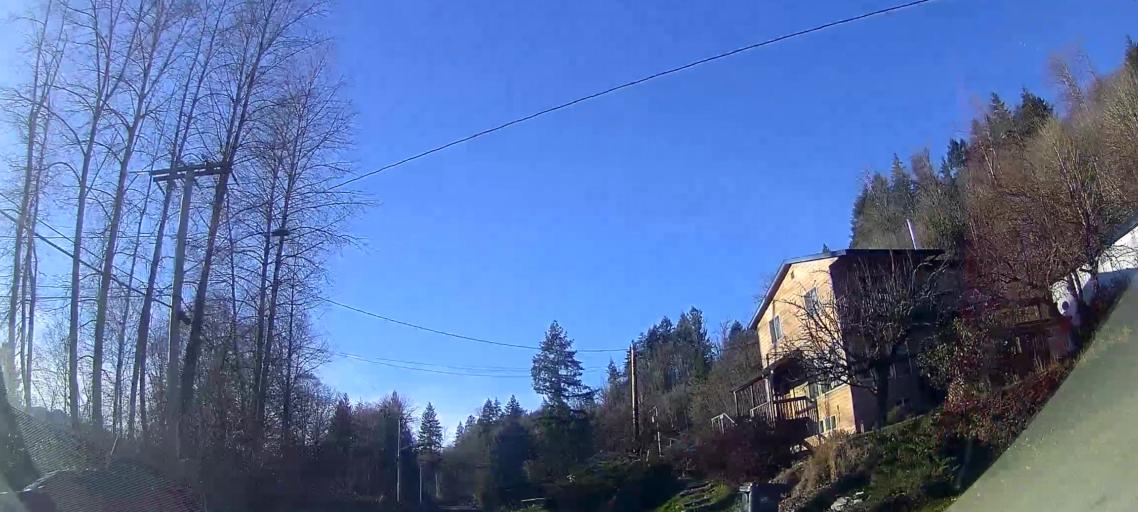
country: US
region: Washington
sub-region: Snohomish County
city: Darrington
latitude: 48.5399
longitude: -121.7551
